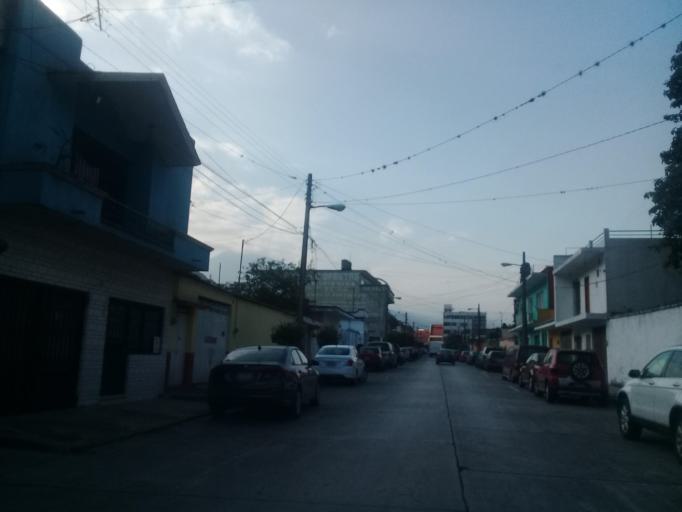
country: MX
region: Veracruz
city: Orizaba
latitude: 18.8485
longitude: -97.1112
